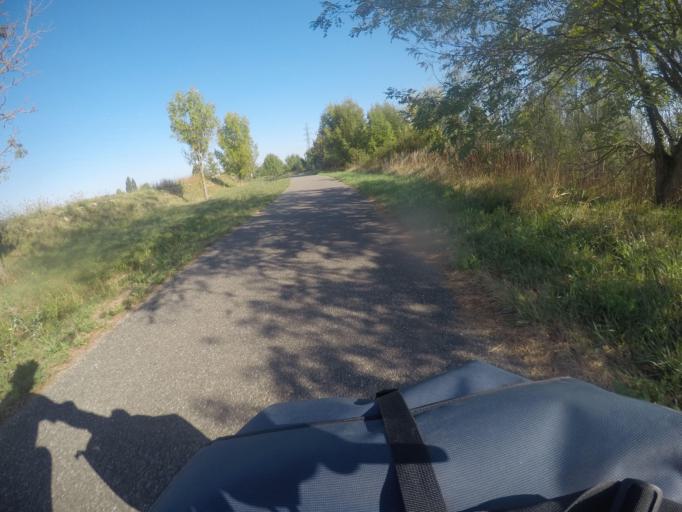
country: FR
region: Alsace
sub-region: Departement du Haut-Rhin
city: Kembs
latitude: 47.7011
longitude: 7.5069
